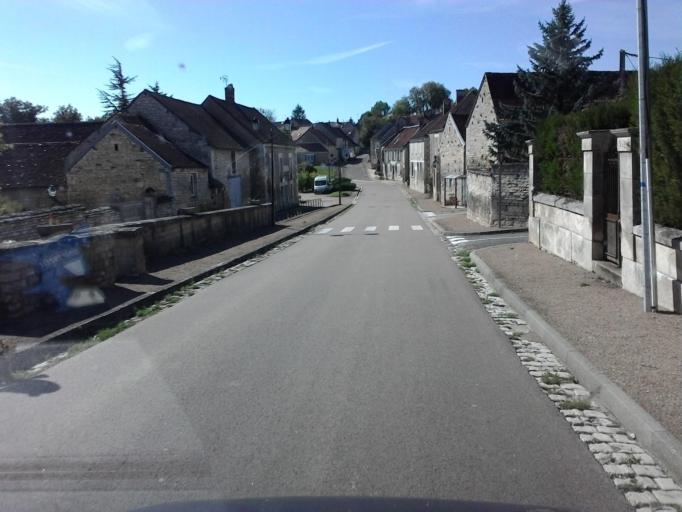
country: FR
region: Bourgogne
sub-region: Departement de l'Yonne
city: Tonnerre
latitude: 47.7937
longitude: 3.9474
